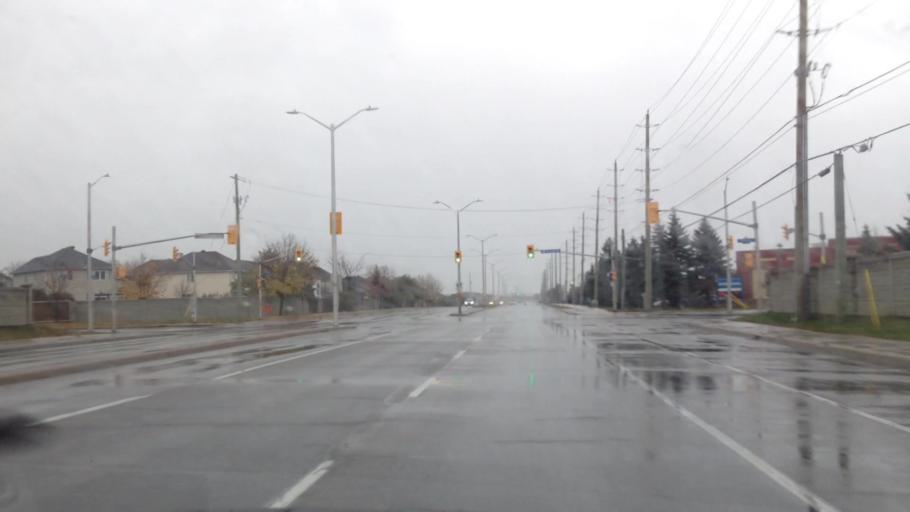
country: CA
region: Ontario
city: Clarence-Rockland
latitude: 45.4687
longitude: -75.4609
